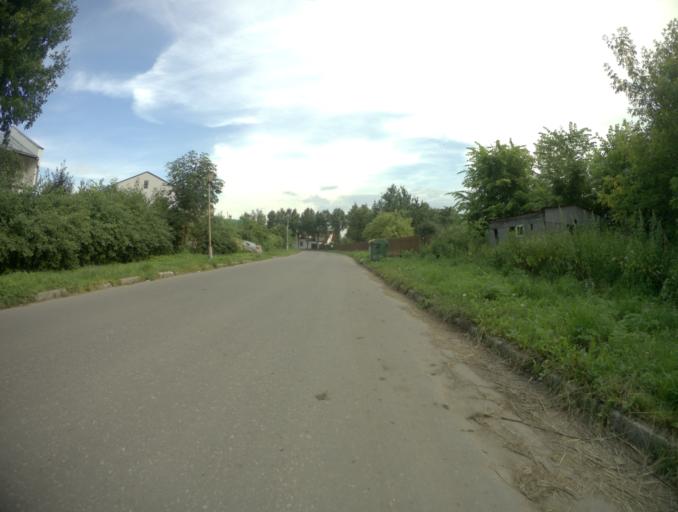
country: RU
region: Vladimir
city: Suzdal'
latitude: 56.4245
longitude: 40.4428
